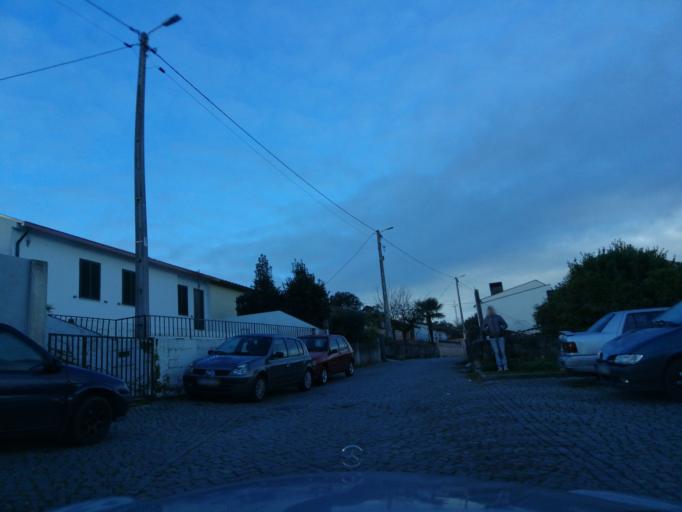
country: PT
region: Braga
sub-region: Braga
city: Braga
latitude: 41.5365
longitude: -8.4185
